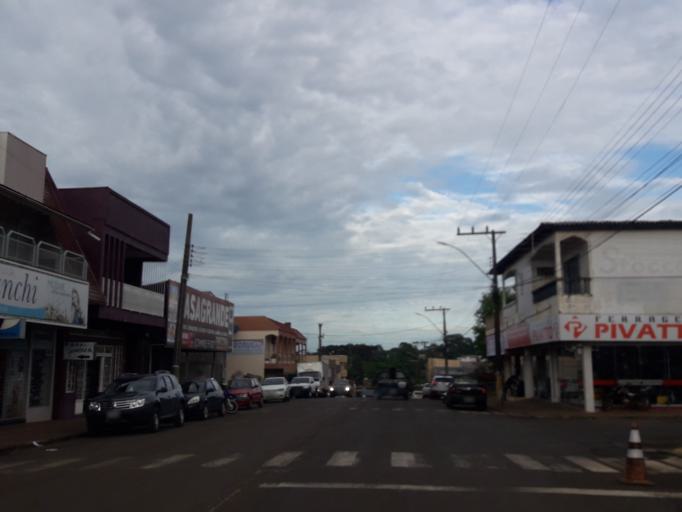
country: AR
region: Misiones
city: Bernardo de Irigoyen
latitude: -26.2554
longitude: -53.6410
